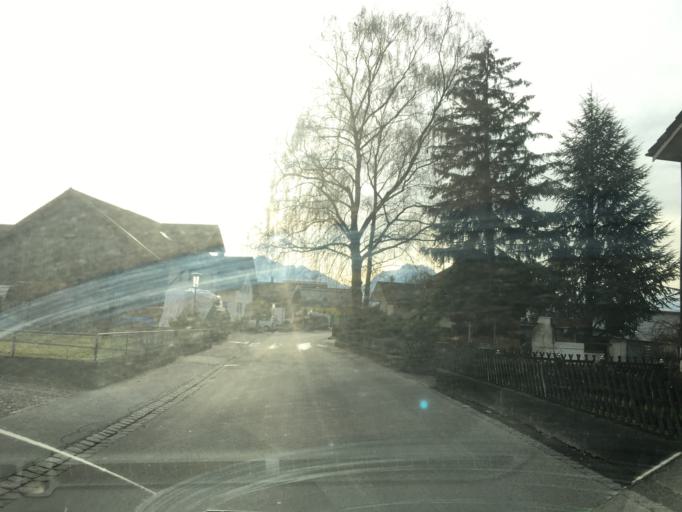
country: AT
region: Vorarlberg
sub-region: Politischer Bezirk Feldkirch
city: Klaus
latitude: 47.3065
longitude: 9.6428
